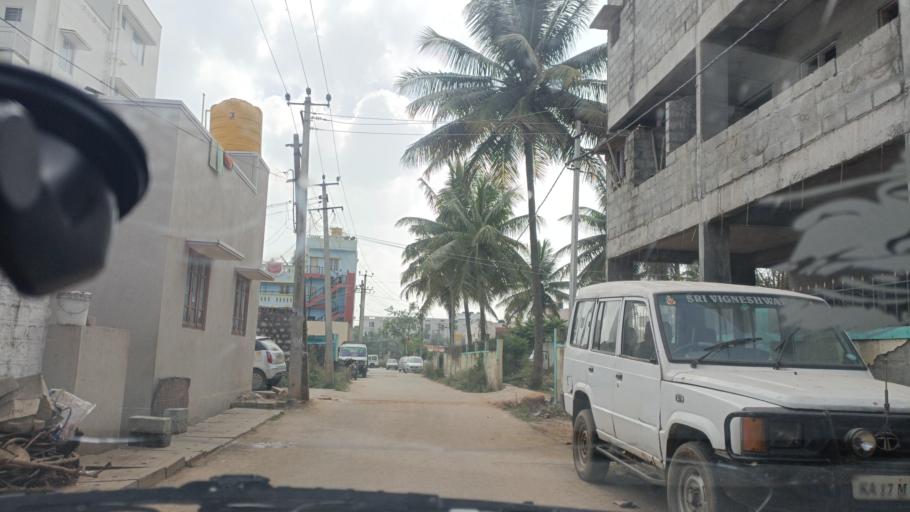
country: IN
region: Karnataka
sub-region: Bangalore Urban
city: Yelahanka
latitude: 13.1643
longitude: 77.6361
